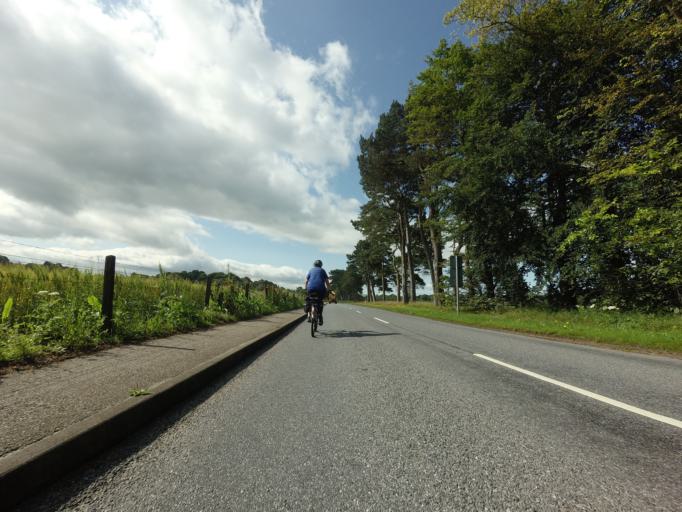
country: GB
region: Scotland
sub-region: Highland
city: Nairn
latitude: 57.5785
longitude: -3.8598
